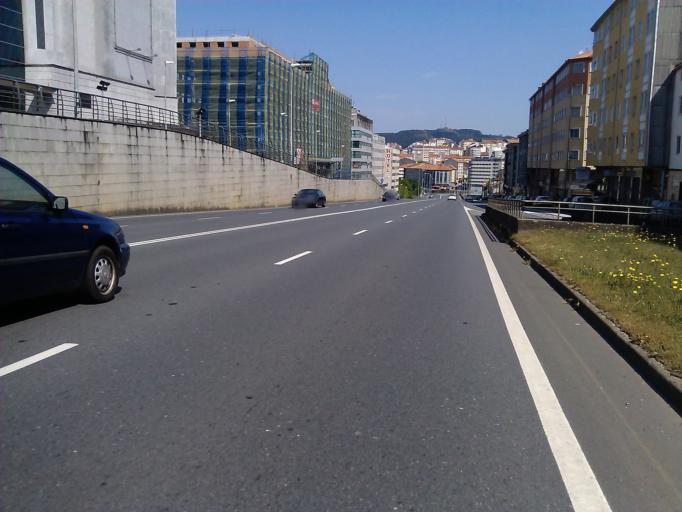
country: ES
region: Galicia
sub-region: Provincia da Coruna
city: Santiago de Compostela
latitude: 42.8629
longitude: -8.5420
